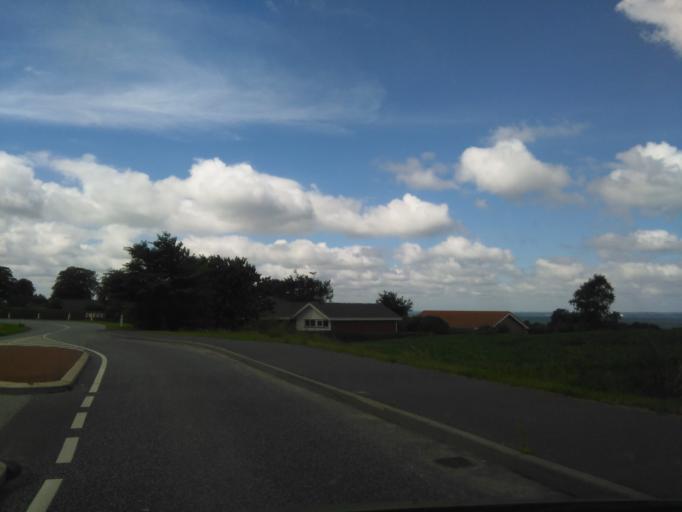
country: DK
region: Central Jutland
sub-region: Syddjurs Kommune
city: Ronde
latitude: 56.2483
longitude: 10.4958
